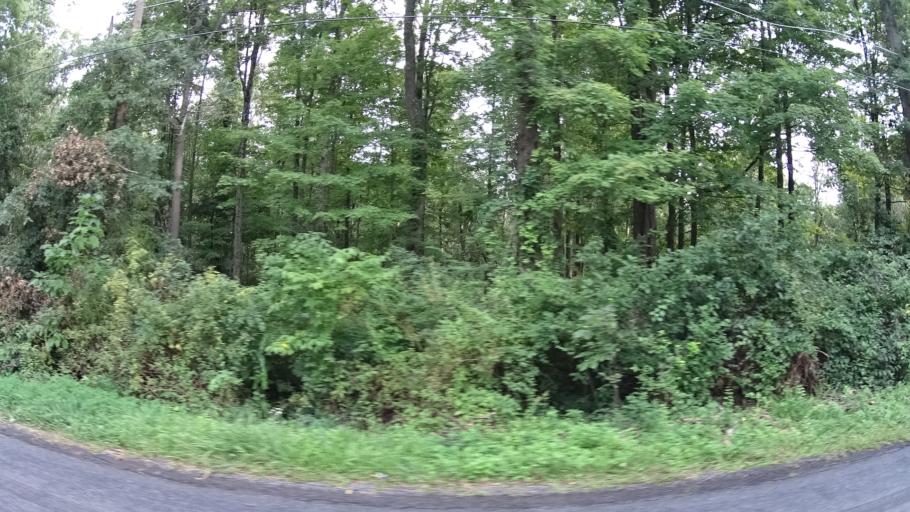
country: US
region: New Jersey
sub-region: Morris County
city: Madison
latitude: 40.7361
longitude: -74.4716
